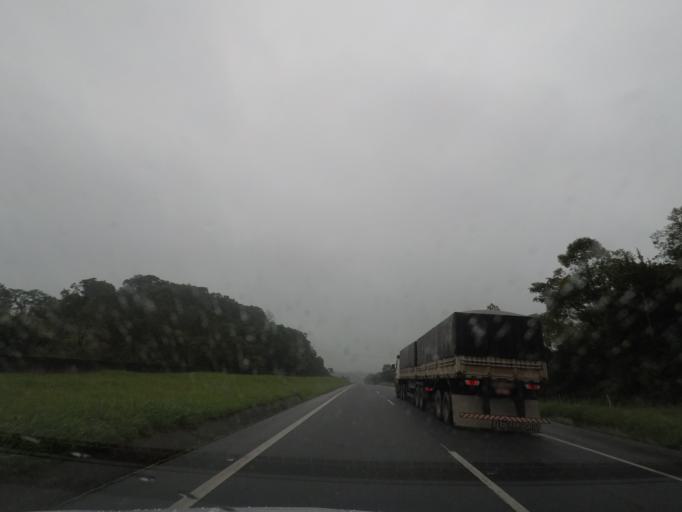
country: BR
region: Sao Paulo
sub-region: Cajati
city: Cajati
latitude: -24.9642
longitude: -48.3421
